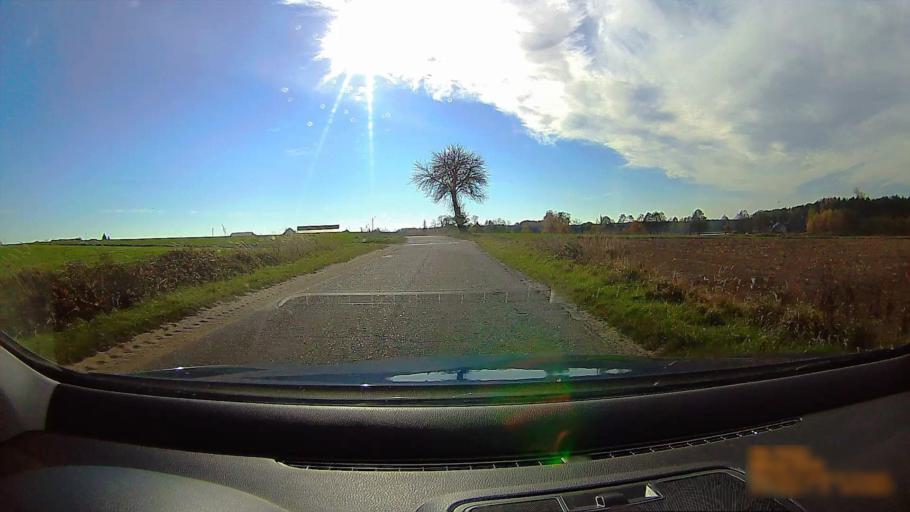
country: PL
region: Greater Poland Voivodeship
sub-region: Powiat ostrzeszowski
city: Doruchow
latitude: 51.3983
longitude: 18.0302
